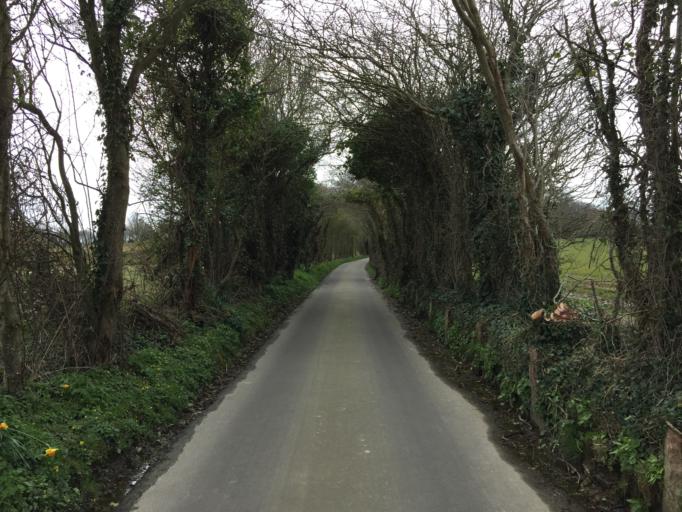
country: JE
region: St Helier
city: Saint Helier
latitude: 49.2033
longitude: -2.0623
